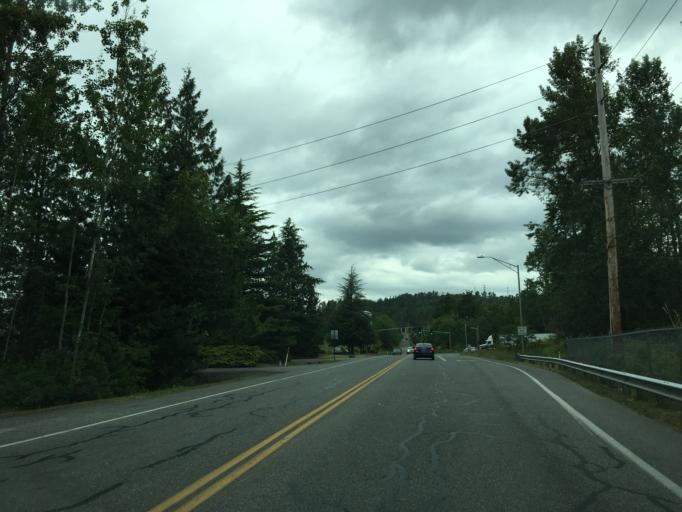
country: US
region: Washington
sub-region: Whatcom County
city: Bellingham
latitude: 48.7881
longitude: -122.4642
